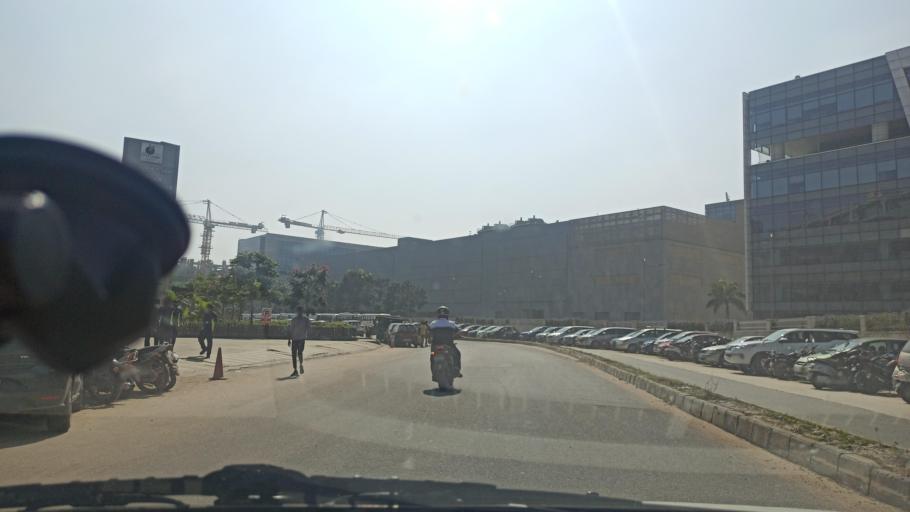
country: IN
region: Karnataka
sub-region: Bangalore Urban
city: Bangalore
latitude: 12.9327
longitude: 77.6915
